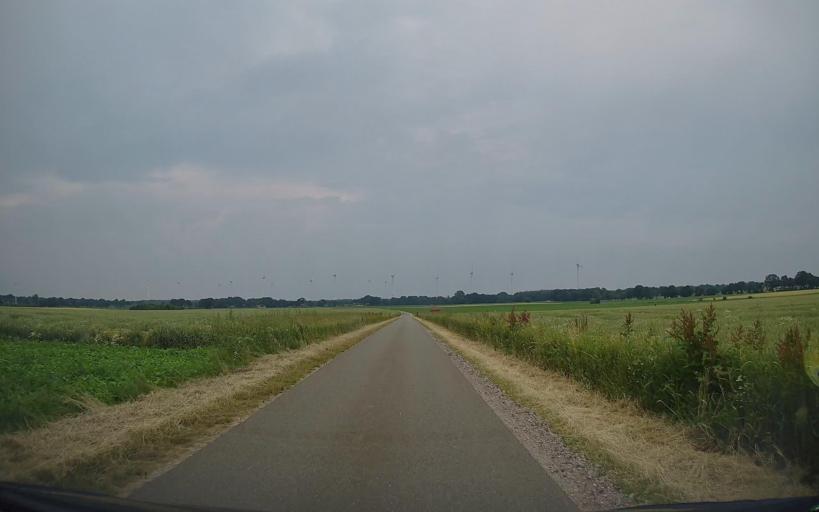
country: DE
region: Lower Saxony
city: Friesoythe
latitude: 53.0288
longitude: 7.8855
